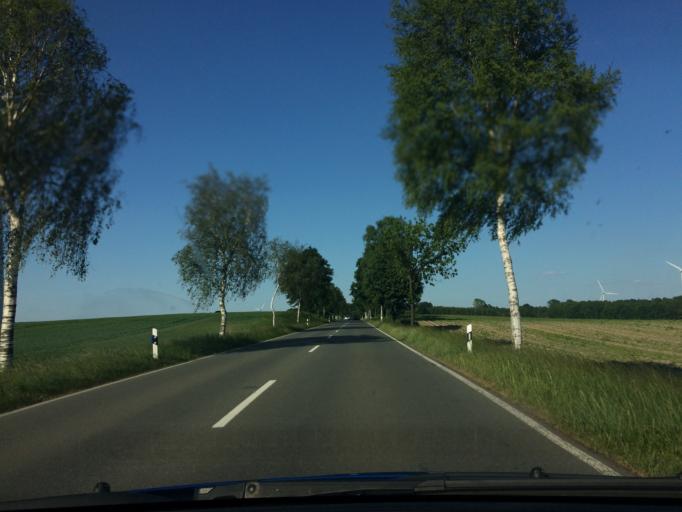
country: DE
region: Lower Saxony
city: Soltau
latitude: 53.0273
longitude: 9.9136
